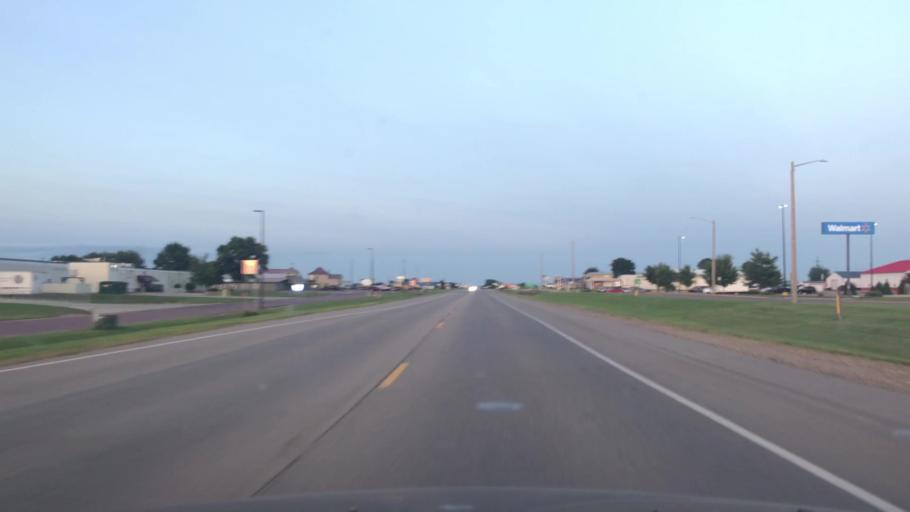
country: US
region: Minnesota
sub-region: Redwood County
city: Redwood Falls
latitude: 44.5414
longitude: -95.0895
